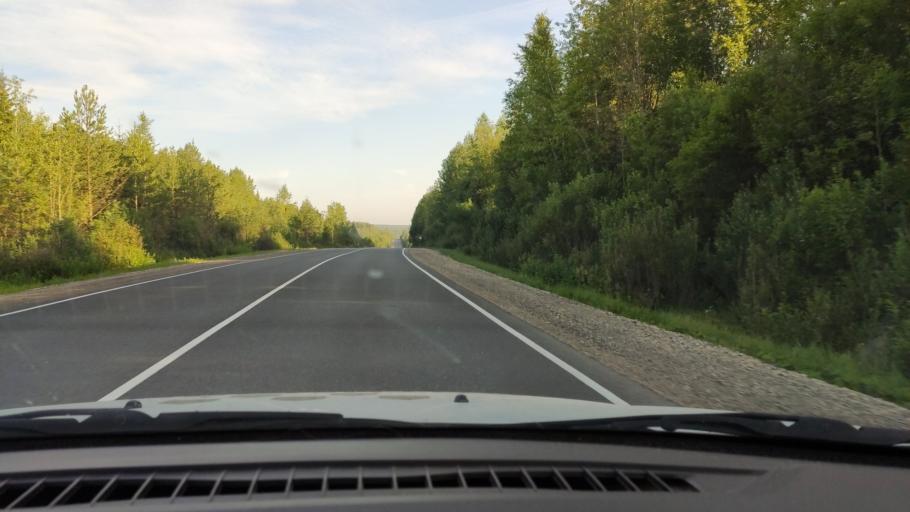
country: RU
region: Kirov
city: Omutninsk
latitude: 58.7089
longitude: 52.1000
